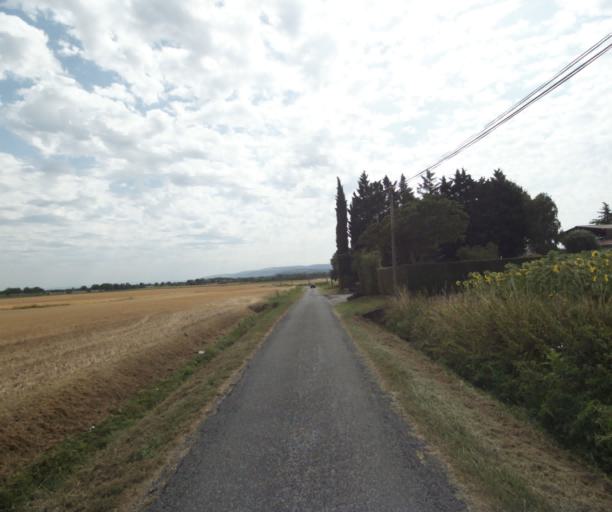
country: FR
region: Midi-Pyrenees
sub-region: Departement de la Haute-Garonne
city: Saint-Felix-Lauragais
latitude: 43.4439
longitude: 1.9116
